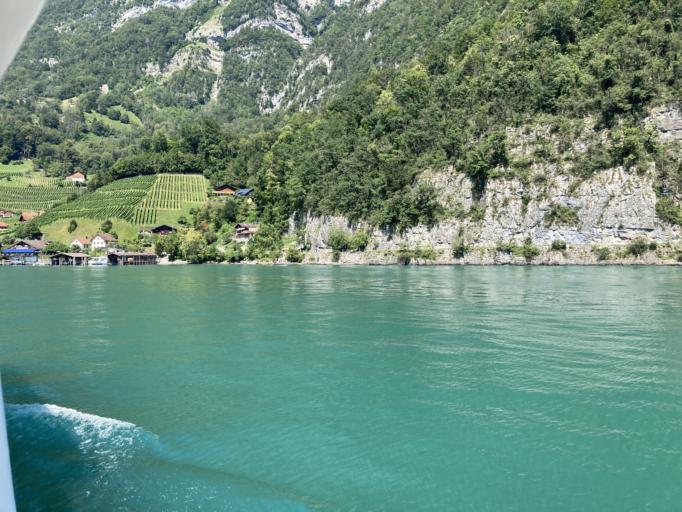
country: CH
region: Saint Gallen
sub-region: Wahlkreis Sarganserland
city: Quarten
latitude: 47.1275
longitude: 9.2203
